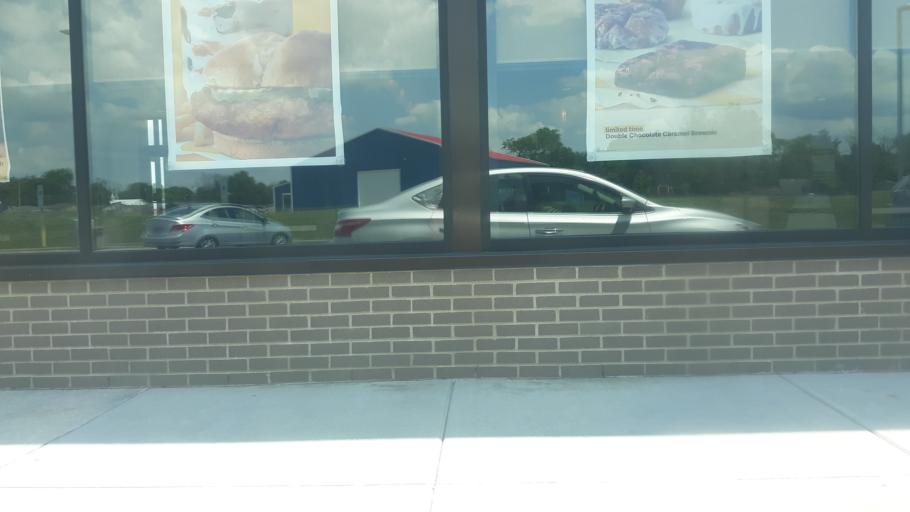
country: US
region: Illinois
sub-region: Saline County
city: Harrisburg
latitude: 37.7296
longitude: -88.5367
